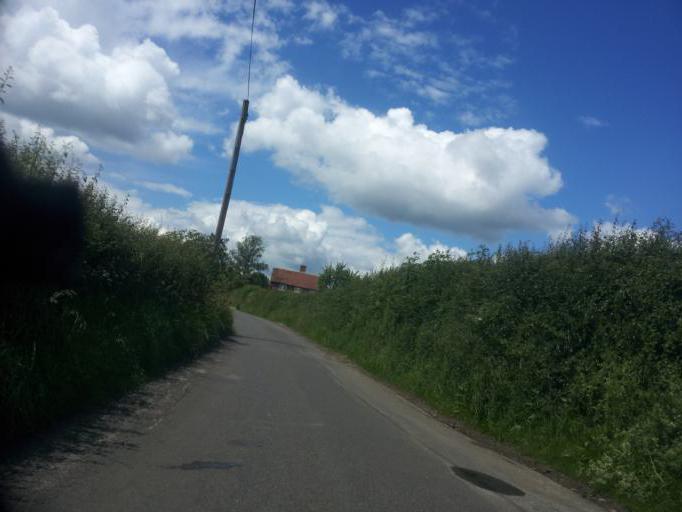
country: GB
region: England
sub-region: Kent
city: West Malling
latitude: 51.3114
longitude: 0.3760
